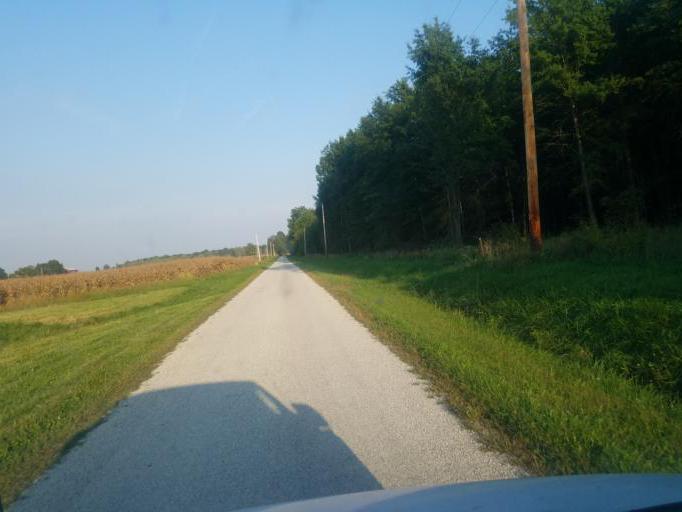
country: US
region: Ohio
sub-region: Crawford County
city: Bucyrus
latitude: 40.9069
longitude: -82.9070
